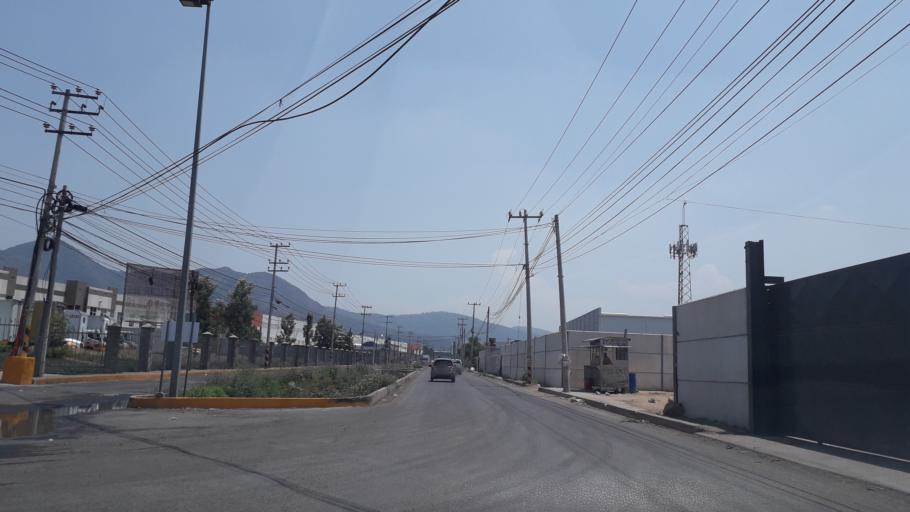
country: MX
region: Mexico
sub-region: Tultitlan
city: Colonia Lazaro Cardenas (Los Hornos)
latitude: 19.6333
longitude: -99.1531
